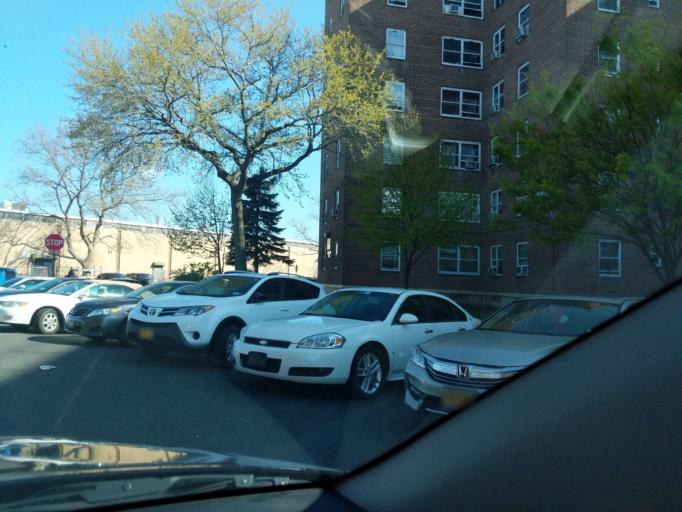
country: US
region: New York
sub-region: Kings County
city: East New York
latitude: 40.6503
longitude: -73.8977
